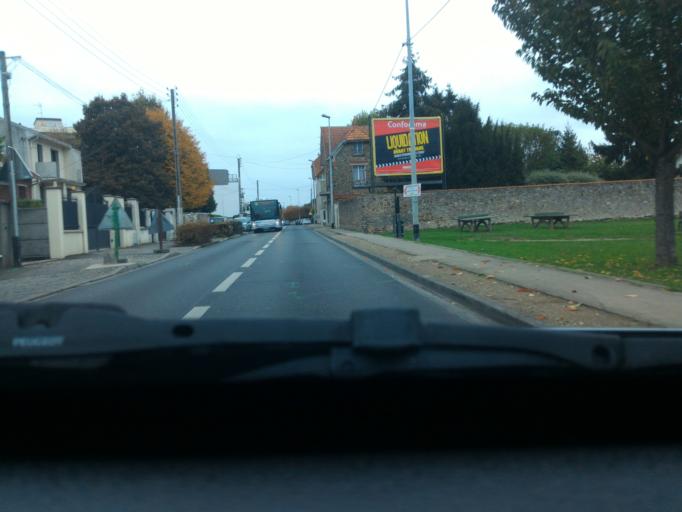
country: FR
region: Ile-de-France
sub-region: Departement du Val-de-Marne
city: Chennevieres-sur-Marne
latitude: 48.7926
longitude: 2.5328
